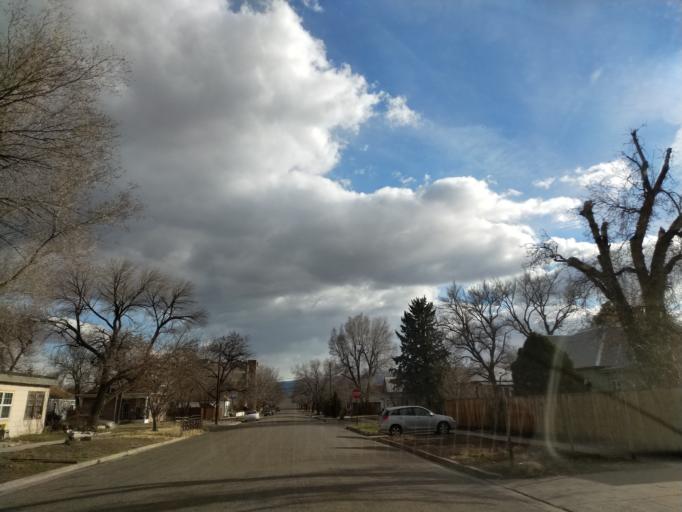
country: US
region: Colorado
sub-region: Mesa County
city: Grand Junction
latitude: 39.0729
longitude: -108.5696
